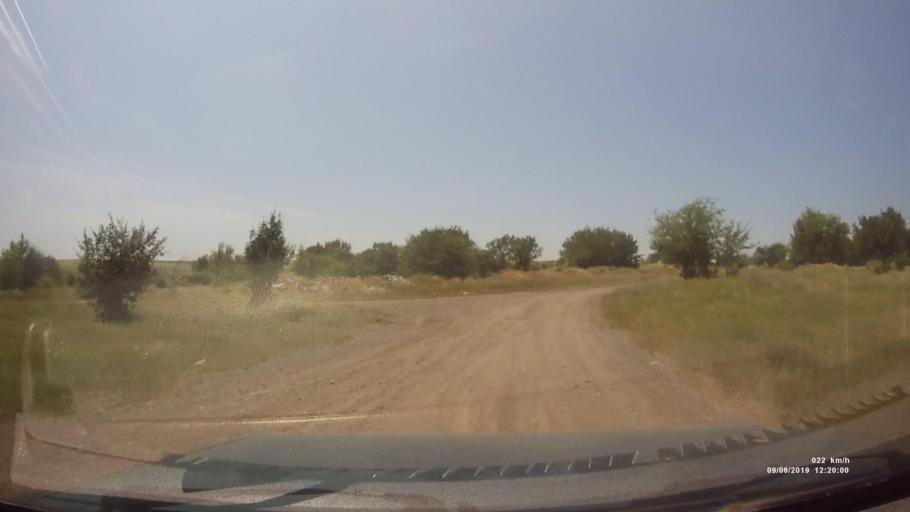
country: RU
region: Rostov
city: Kamensk-Shakhtinskiy
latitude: 48.2519
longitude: 40.3033
